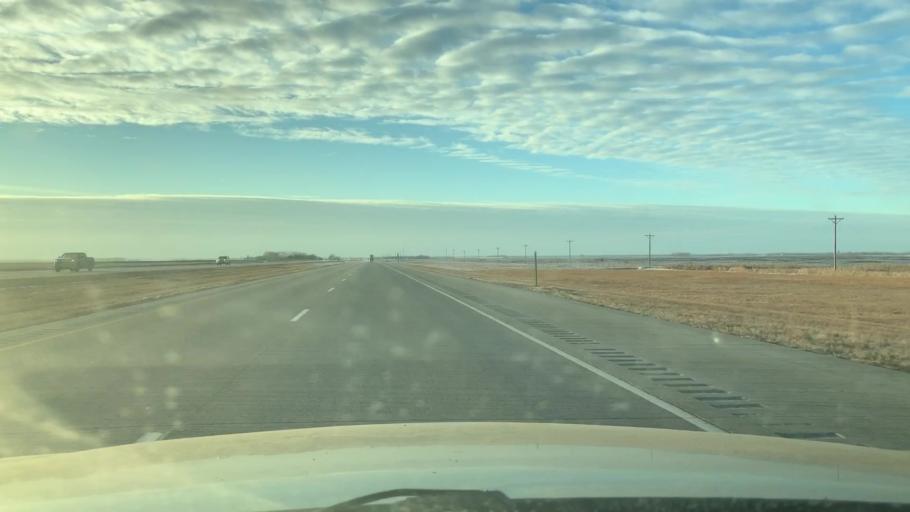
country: US
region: North Dakota
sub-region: Cass County
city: Casselton
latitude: 46.8761
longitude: -97.2754
